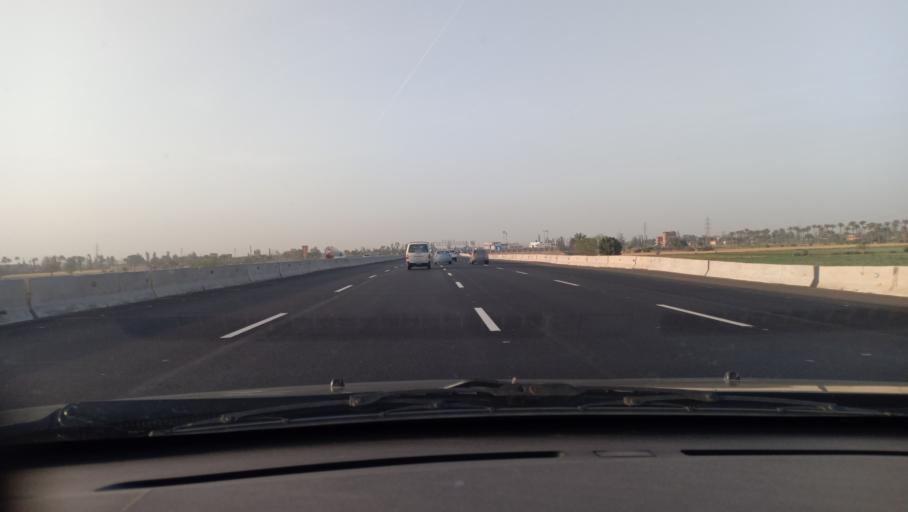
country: EG
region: Muhafazat al Qalyubiyah
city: Toukh
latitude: 30.2994
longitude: 31.2191
